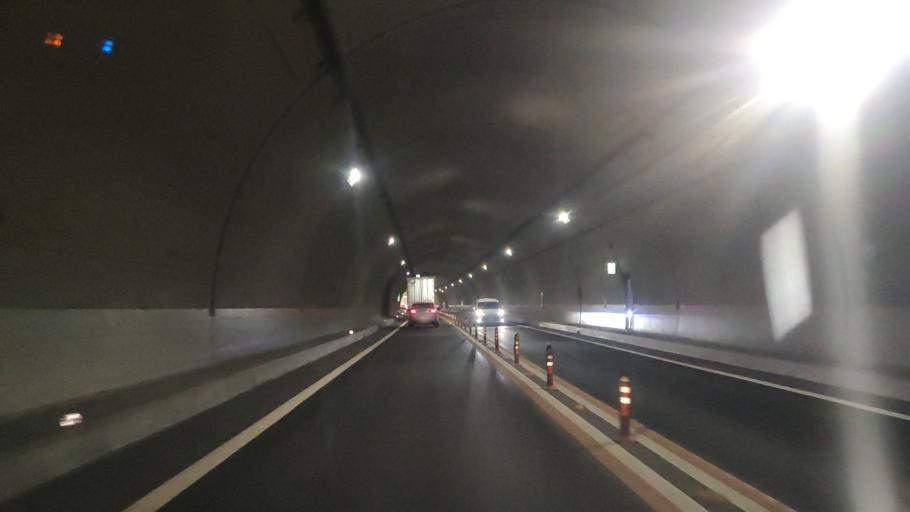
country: JP
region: Fukuoka
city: Kanda
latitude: 33.7738
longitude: 130.9688
